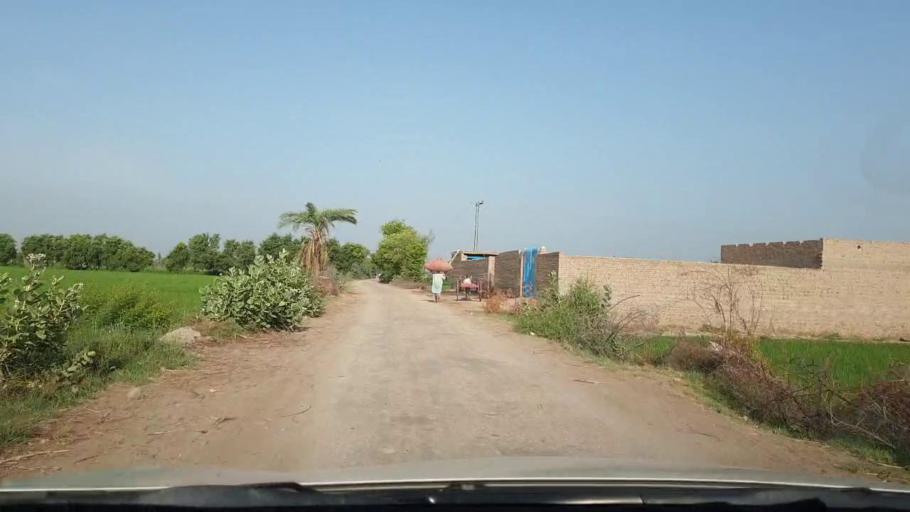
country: PK
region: Sindh
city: Larkana
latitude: 27.5452
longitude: 68.2649
